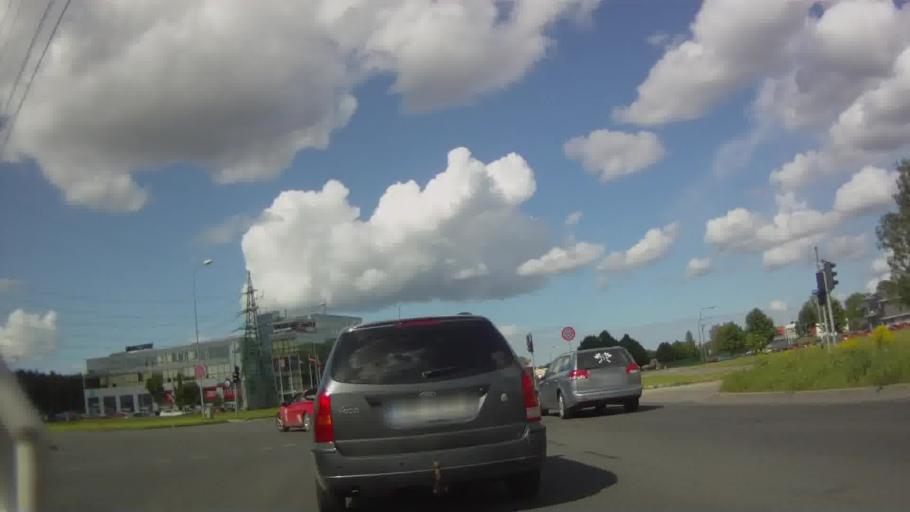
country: LV
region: Stopini
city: Ulbroka
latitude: 56.9521
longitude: 24.2208
